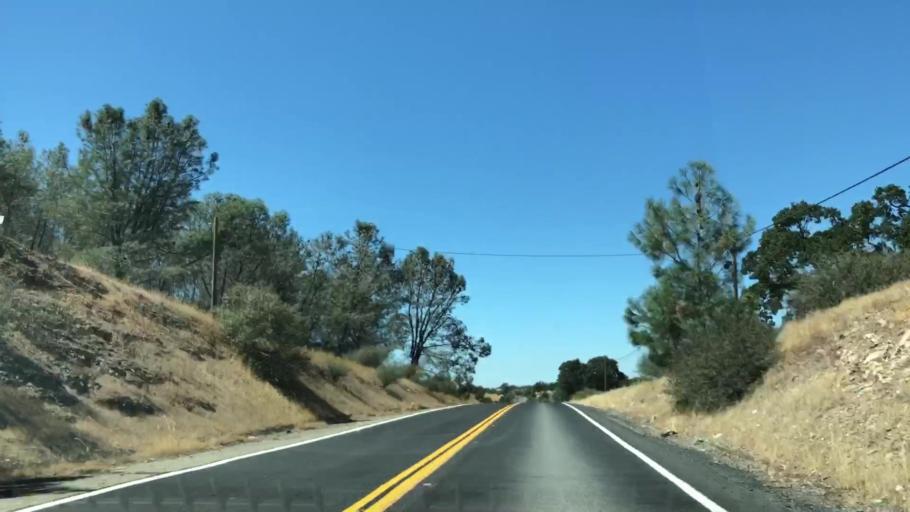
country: US
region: California
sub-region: Tuolumne County
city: Jamestown
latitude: 37.8883
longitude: -120.5282
